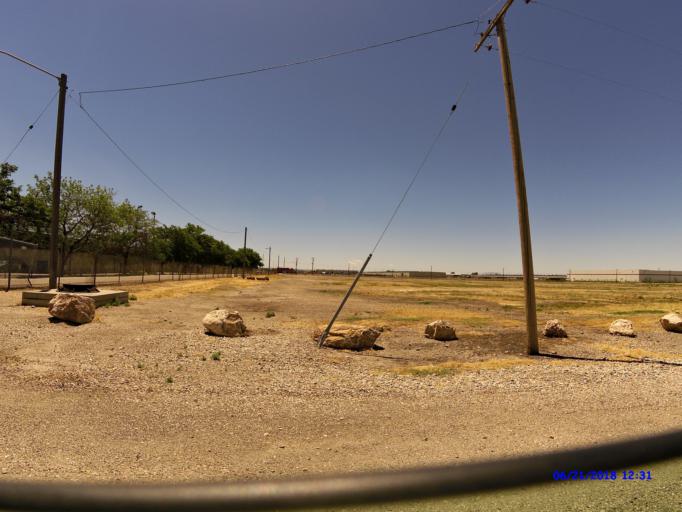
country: US
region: Utah
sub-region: Weber County
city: Harrisville
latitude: 41.2762
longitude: -112.0000
